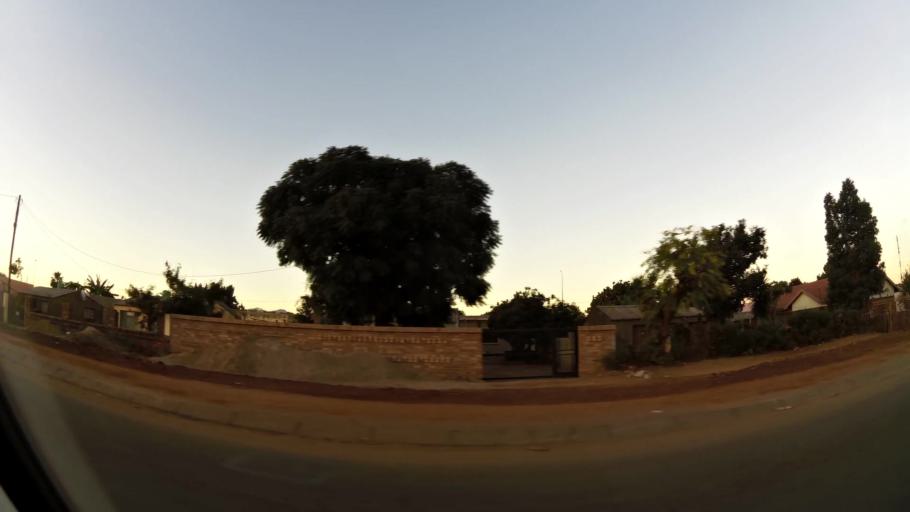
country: ZA
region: Limpopo
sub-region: Waterberg District Municipality
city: Mokopane
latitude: -24.1462
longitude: 28.9768
